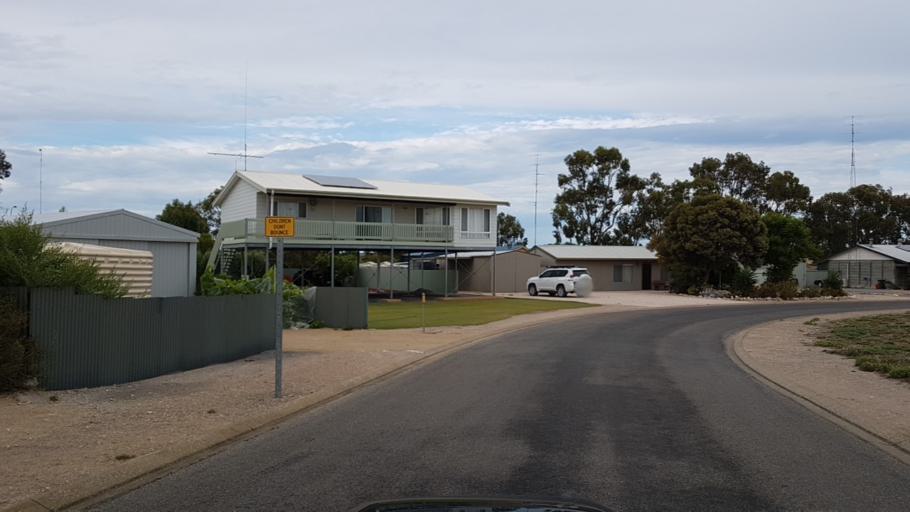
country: AU
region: South Australia
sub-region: Yorke Peninsula
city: Port Victoria
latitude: -34.9105
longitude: 137.0528
